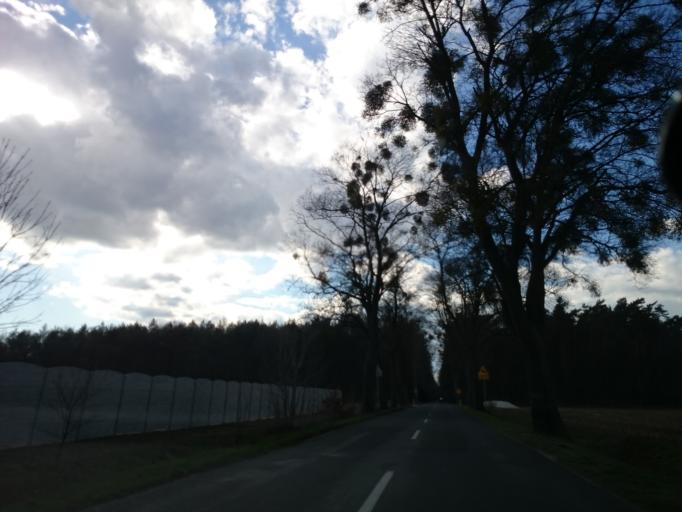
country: PL
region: Opole Voivodeship
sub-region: Powiat opolski
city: Niemodlin
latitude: 50.6233
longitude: 17.5654
